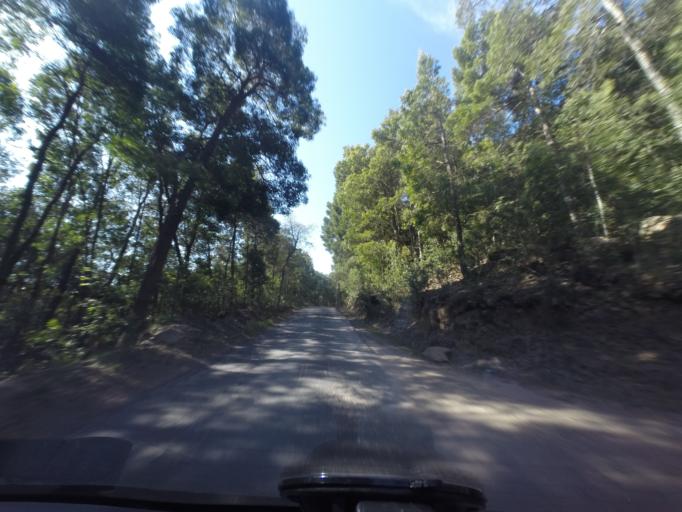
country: PT
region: Lisbon
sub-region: Sintra
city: Colares
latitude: 38.7719
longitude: -9.4360
